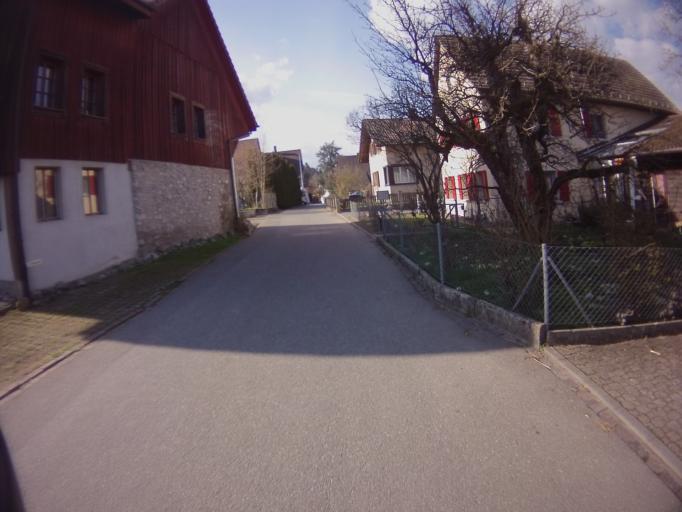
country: CH
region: Aargau
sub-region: Bezirk Baden
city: Neuenhof
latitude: 47.4439
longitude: 8.3293
